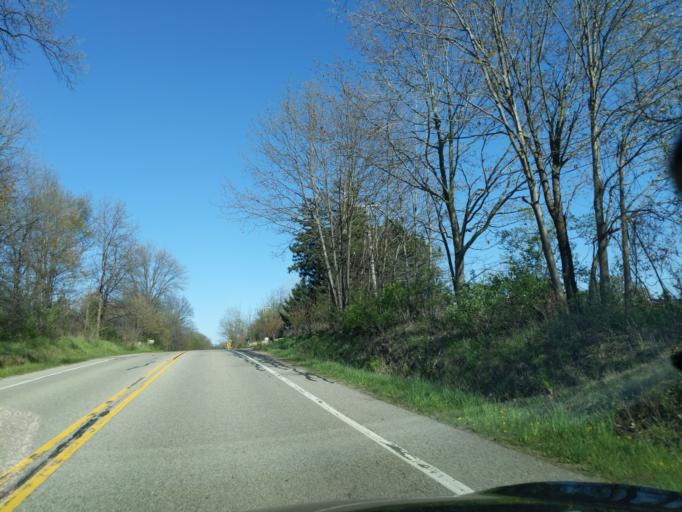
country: US
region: Michigan
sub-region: Kent County
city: Lowell
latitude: 42.8854
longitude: -85.4158
